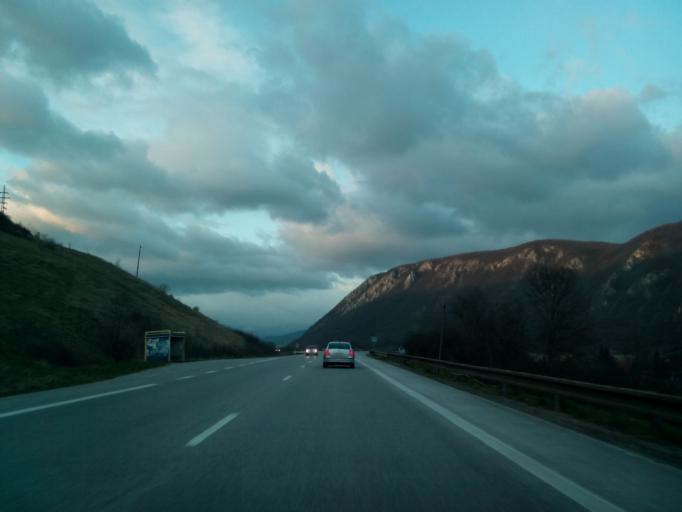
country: SK
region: Kosicky
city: Roznava
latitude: 48.5870
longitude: 20.4661
